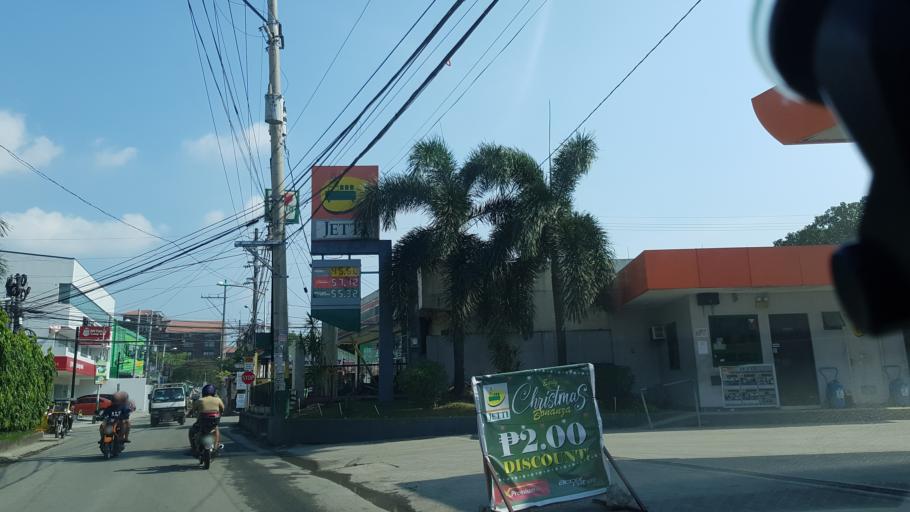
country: PH
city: Sambayanihan People's Village
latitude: 14.4981
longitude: 121.0128
